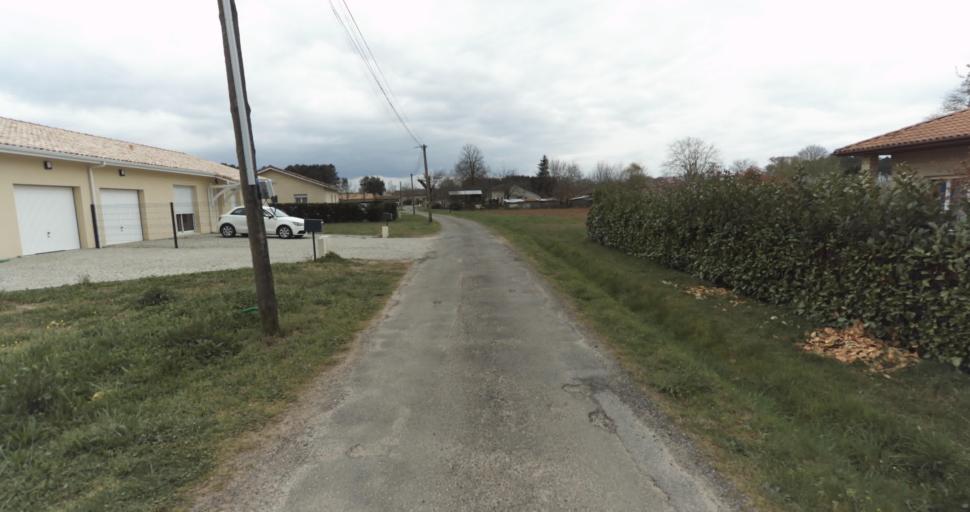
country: FR
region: Aquitaine
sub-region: Departement des Landes
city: Roquefort
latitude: 44.0243
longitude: -0.3348
